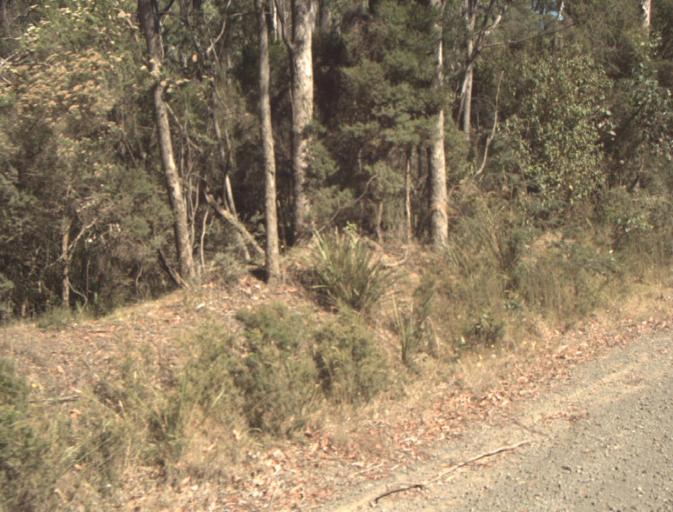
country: AU
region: Tasmania
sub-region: Launceston
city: Mayfield
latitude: -41.3494
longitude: 147.2181
